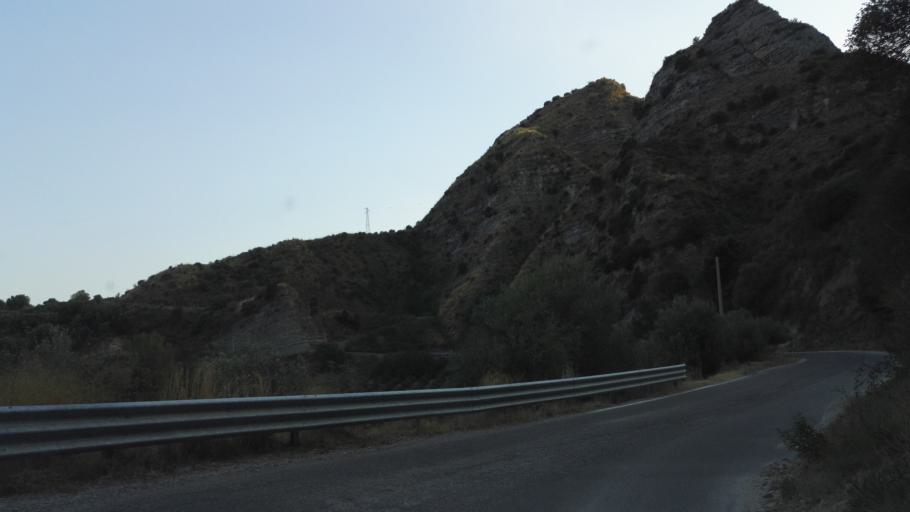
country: IT
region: Calabria
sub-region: Provincia di Reggio Calabria
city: Caulonia
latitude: 38.3997
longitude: 16.4139
